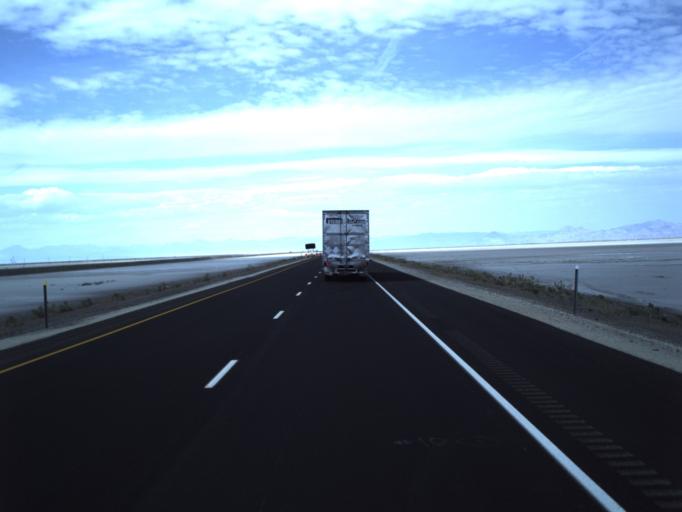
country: US
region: Utah
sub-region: Tooele County
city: Wendover
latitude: 40.7332
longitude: -113.5616
